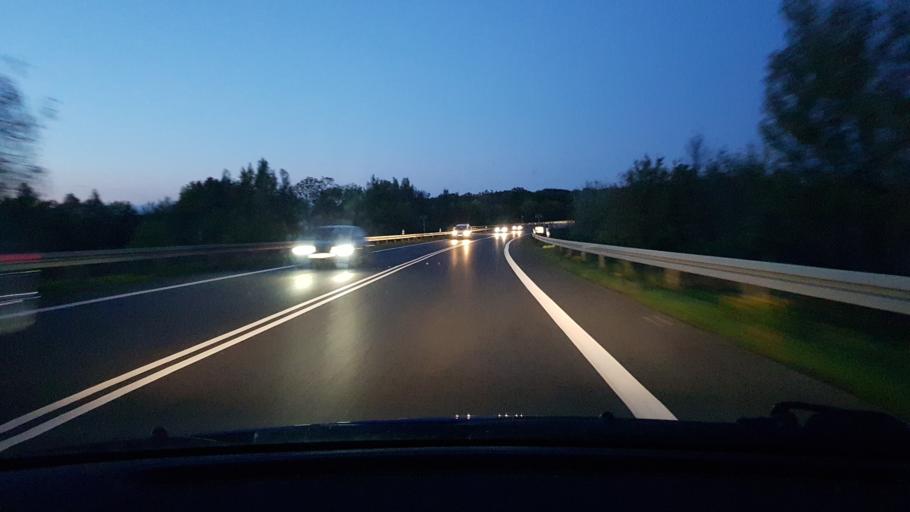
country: DE
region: Lower Saxony
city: Vordorf
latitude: 52.3368
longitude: 10.5249
